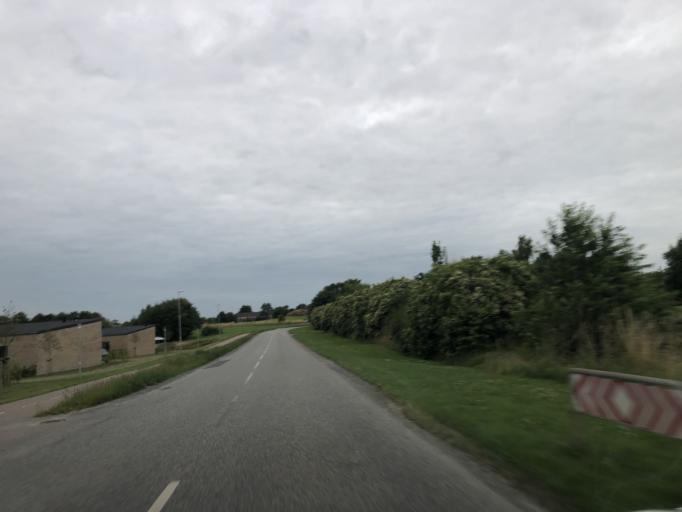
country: DK
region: South Denmark
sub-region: Vejle Kommune
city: Jelling
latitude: 55.7457
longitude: 9.4132
